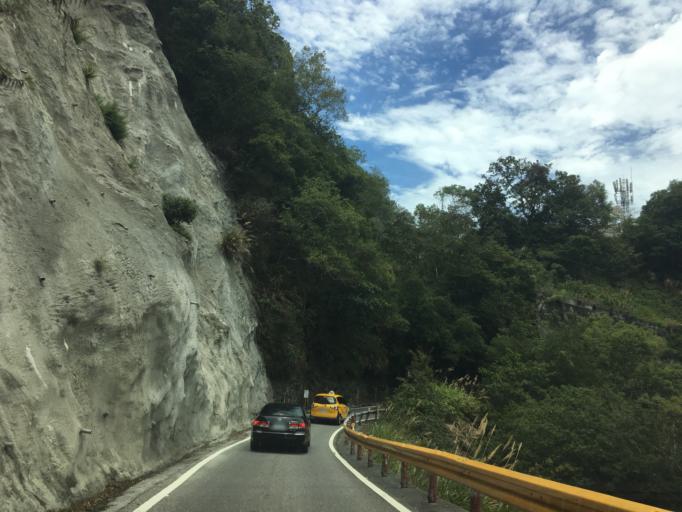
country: TW
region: Taiwan
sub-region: Hualien
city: Hualian
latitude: 24.1908
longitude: 121.4839
